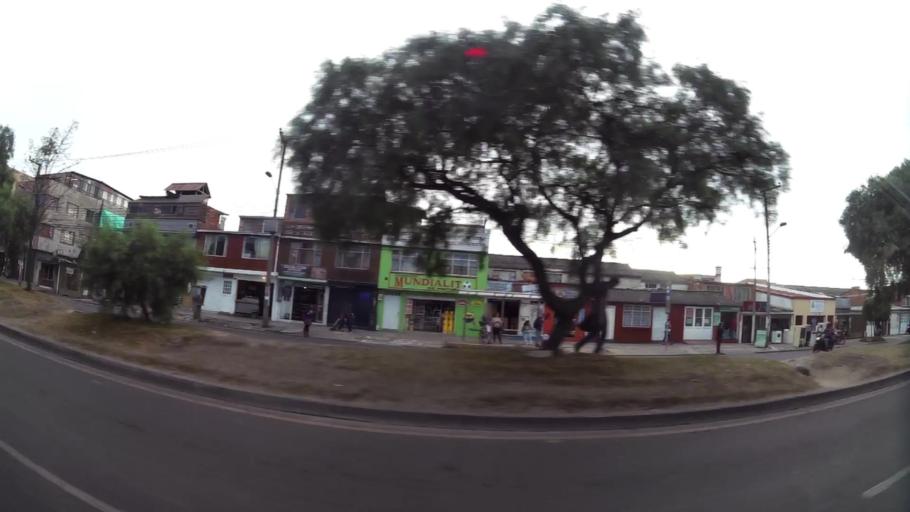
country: CO
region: Cundinamarca
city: Soacha
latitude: 4.6192
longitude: -74.1648
